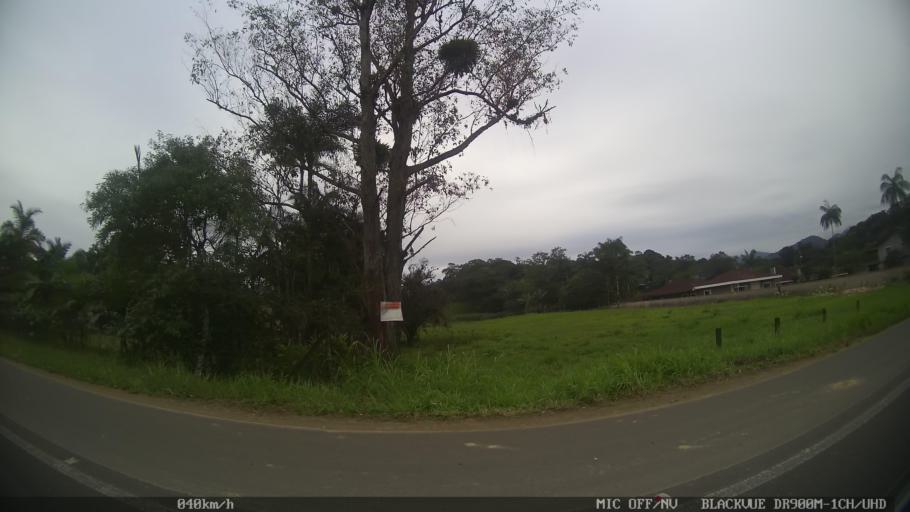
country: BR
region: Santa Catarina
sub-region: Joinville
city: Joinville
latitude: -26.3016
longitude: -48.9205
